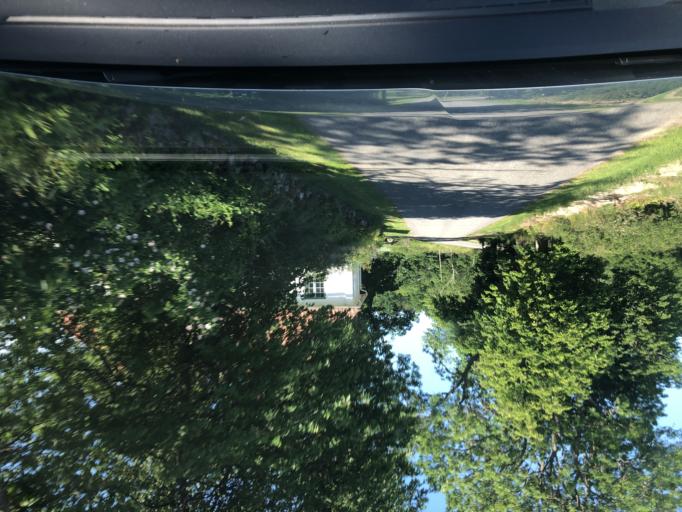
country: SE
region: Blekinge
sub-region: Karlshamns Kommun
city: Morrum
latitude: 56.1738
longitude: 14.7153
